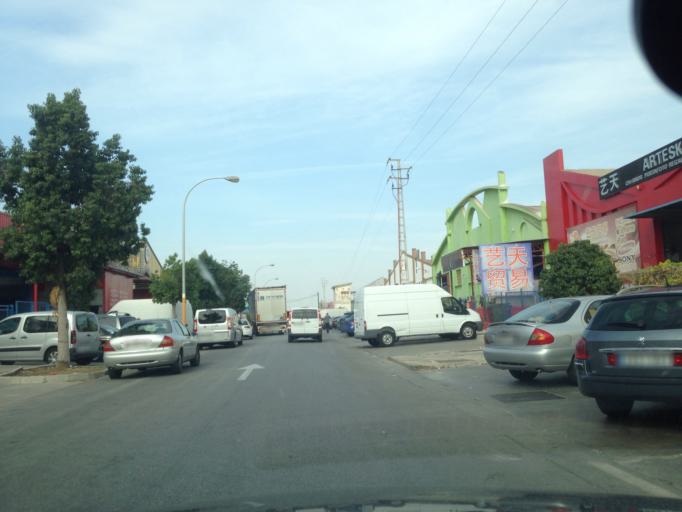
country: ES
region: Andalusia
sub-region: Provincia de Malaga
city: Malaga
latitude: 36.6896
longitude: -4.4743
